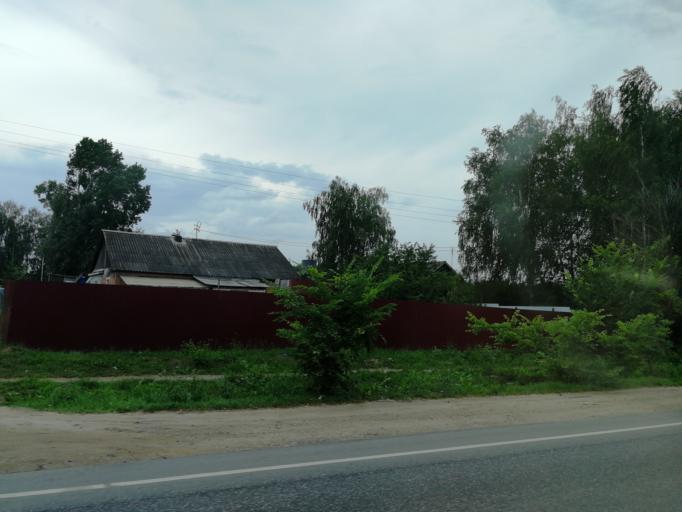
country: RU
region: Tula
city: Bolokhovo
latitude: 54.1124
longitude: 37.7470
